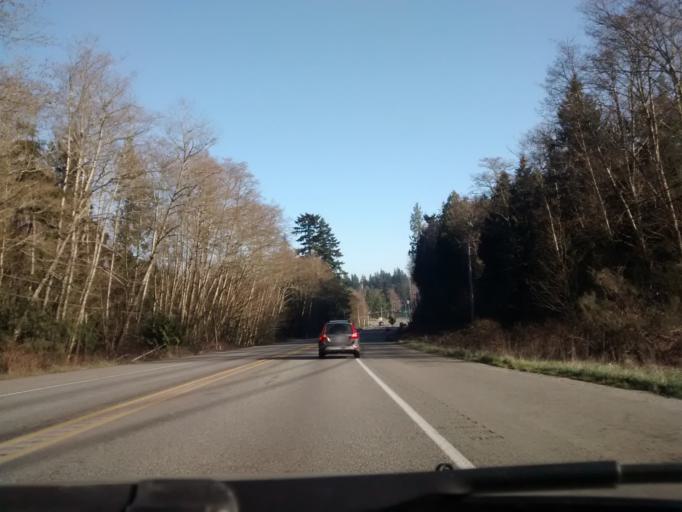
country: US
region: Washington
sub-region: Kitsap County
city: Lofall
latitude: 47.8140
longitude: -122.6455
